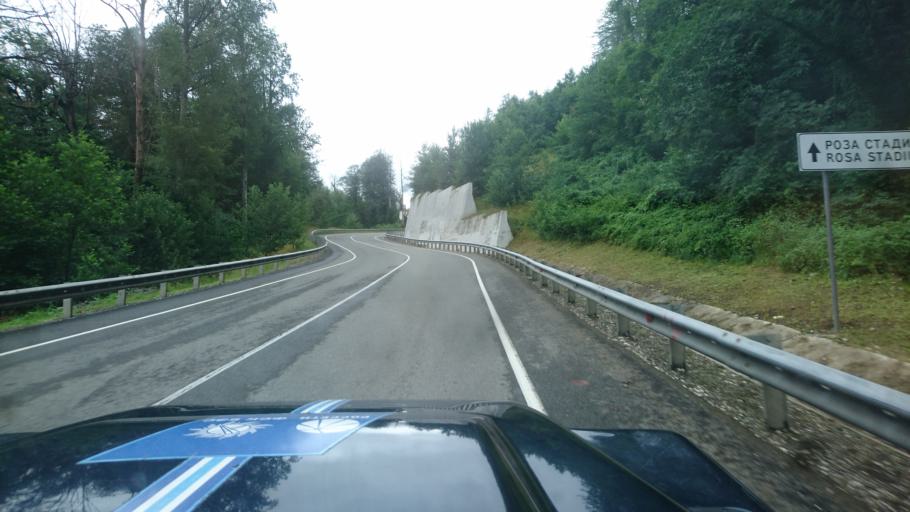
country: RU
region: Krasnodarskiy
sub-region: Sochi City
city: Krasnaya Polyana
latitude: 43.6666
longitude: 40.2955
